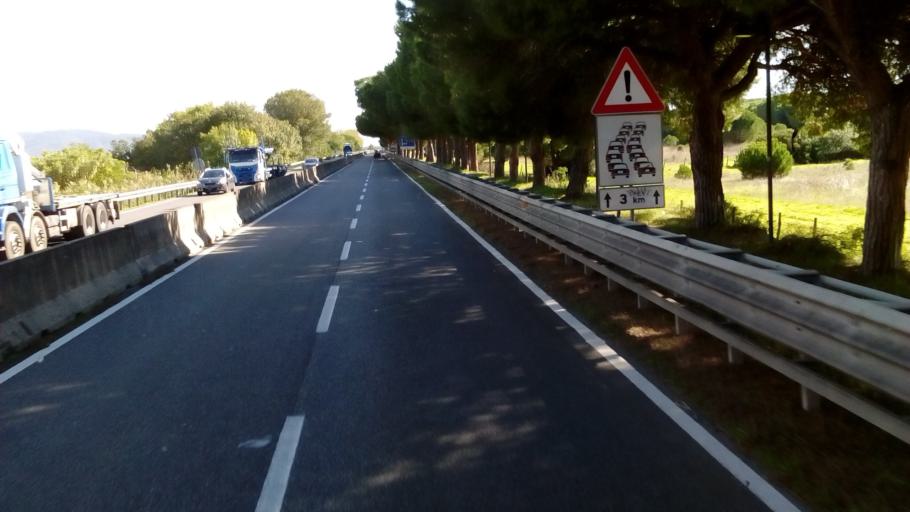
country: IT
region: Tuscany
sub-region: Provincia di Grosseto
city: Fonteblanda
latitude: 42.5419
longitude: 11.1800
